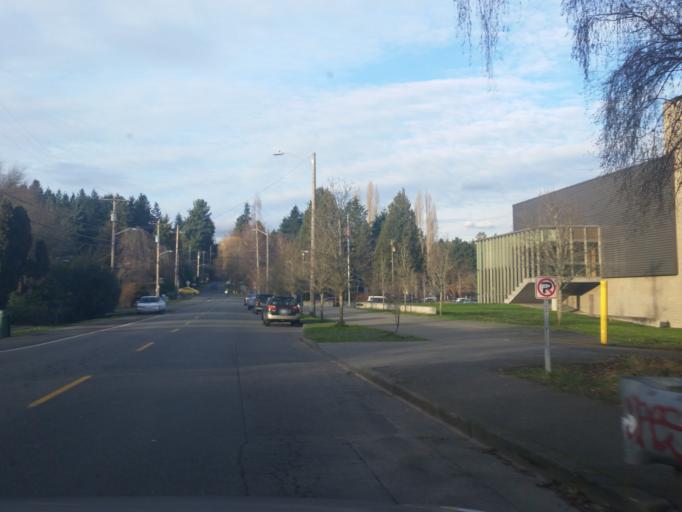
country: US
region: Washington
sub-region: King County
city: Lake Forest Park
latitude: 47.7068
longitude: -122.2962
